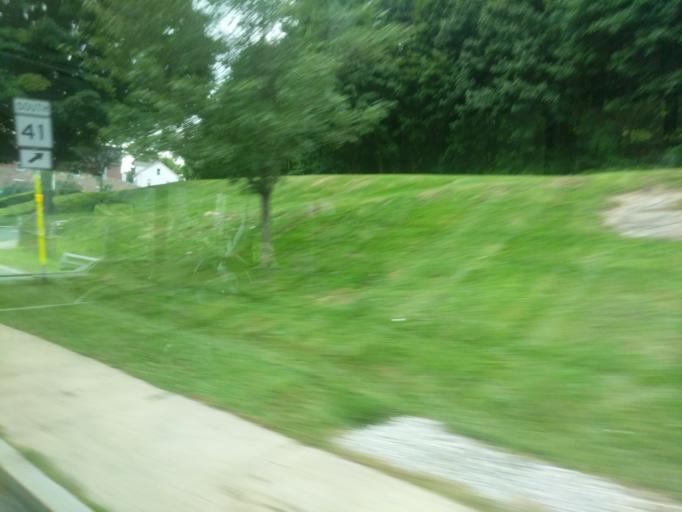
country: US
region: Massachusetts
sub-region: Berkshire County
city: Great Barrington
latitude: 42.2019
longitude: -73.3583
